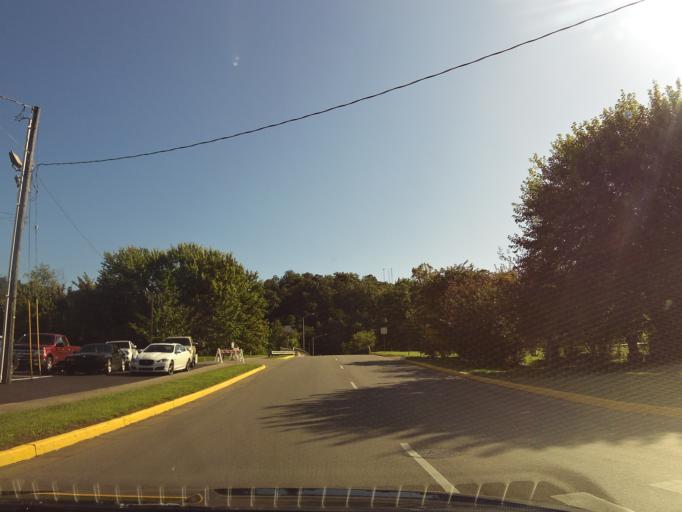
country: US
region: Kentucky
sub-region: Whitley County
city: Williamsburg
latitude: 36.7429
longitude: -84.1585
